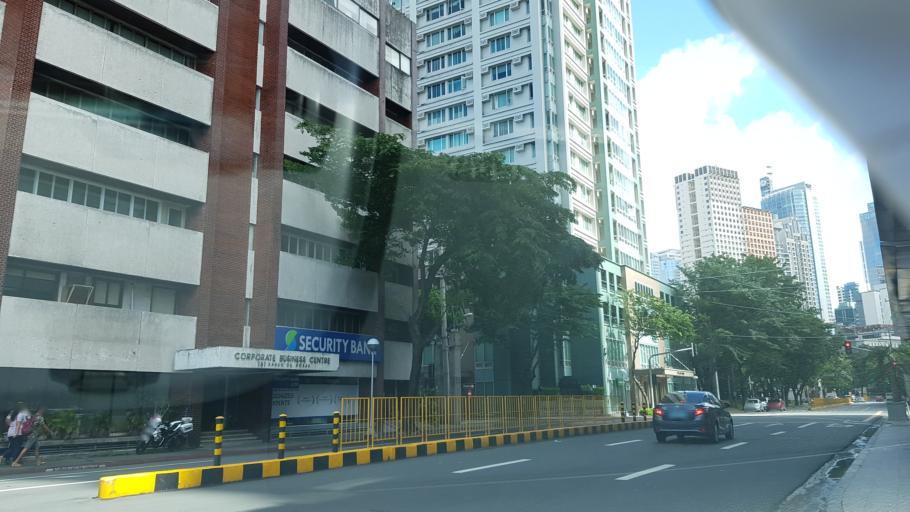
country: PH
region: Metro Manila
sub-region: Makati City
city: Makati City
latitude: 14.5509
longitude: 121.0191
